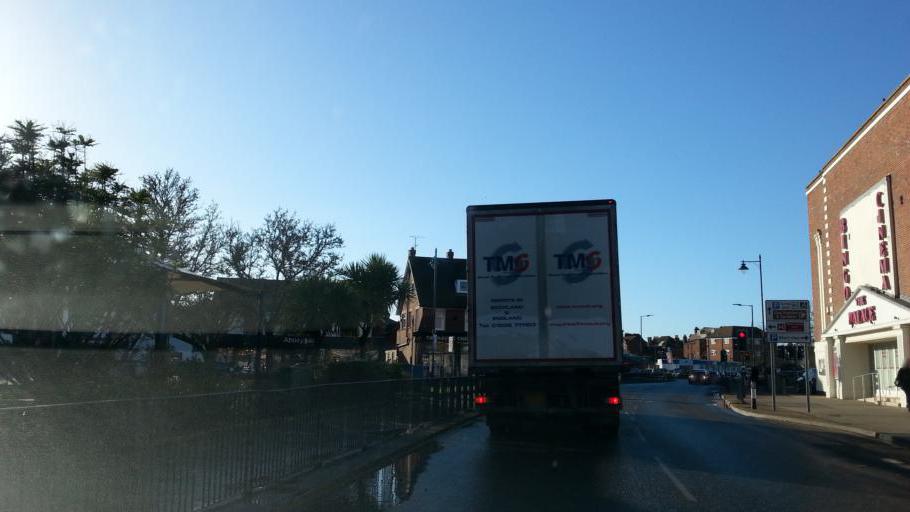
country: GB
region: England
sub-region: Suffolk
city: Felixstowe
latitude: 51.9642
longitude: 1.3517
